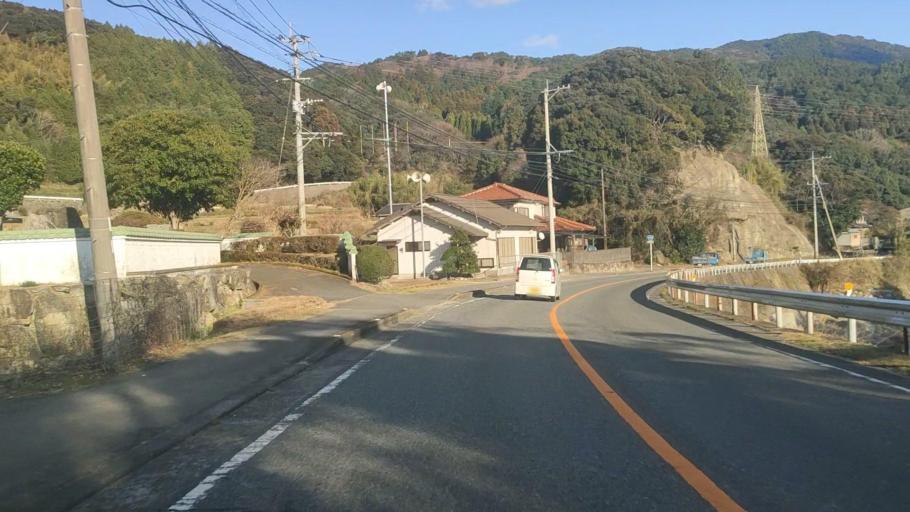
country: JP
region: Saga Prefecture
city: Saga-shi
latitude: 33.3433
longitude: 130.2513
